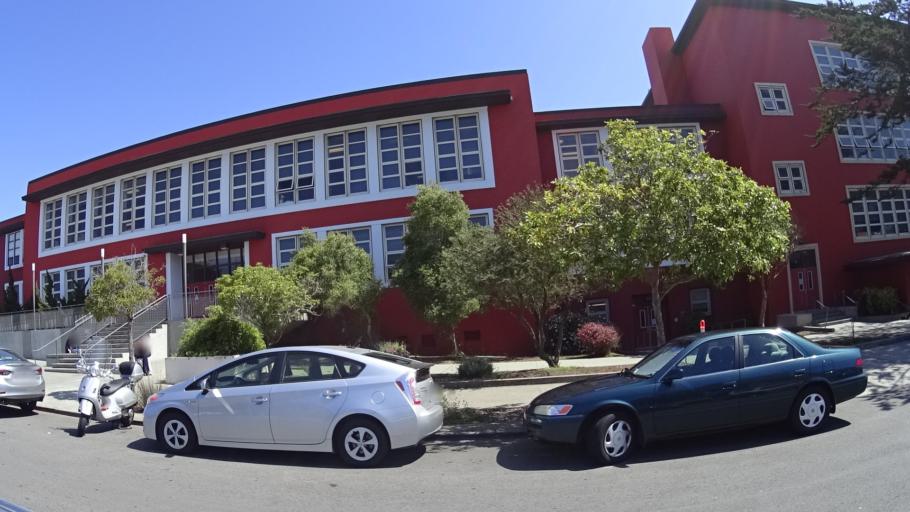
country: US
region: California
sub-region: San Mateo County
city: Daly City
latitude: 37.7479
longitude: -122.4815
